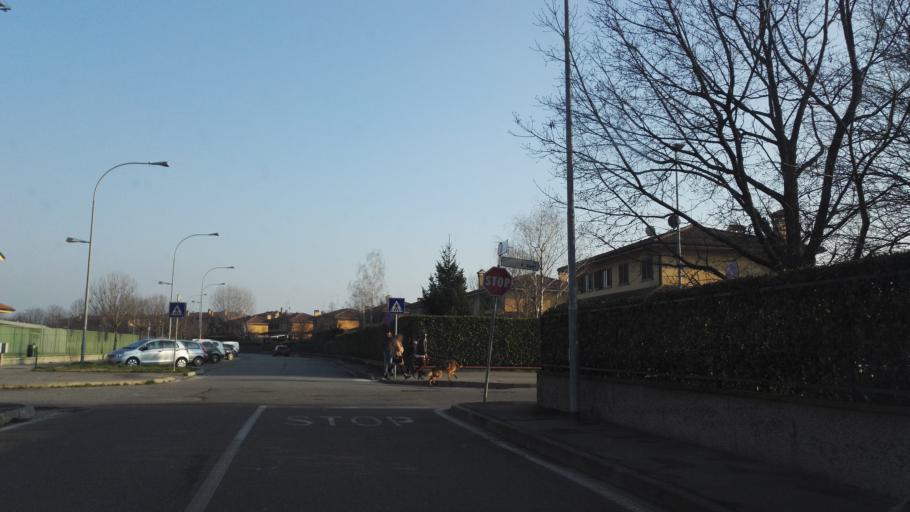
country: IT
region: Lombardy
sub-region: Citta metropolitana di Milano
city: Tribiano
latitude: 45.4166
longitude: 9.3720
